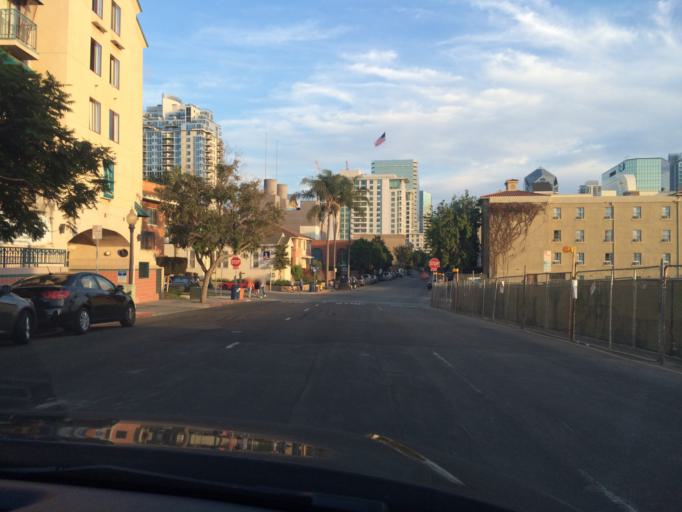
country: US
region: California
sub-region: San Diego County
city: San Diego
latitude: 32.7235
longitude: -117.1675
